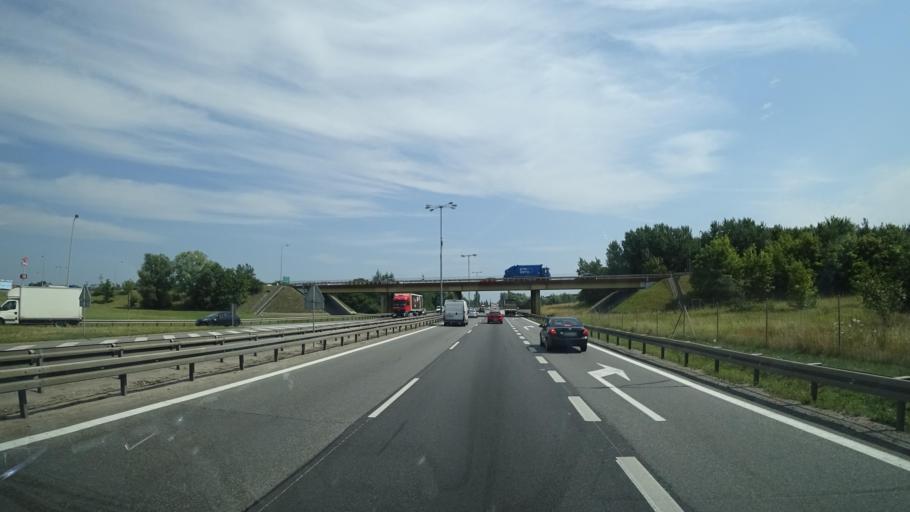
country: PL
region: Pomeranian Voivodeship
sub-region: Powiat gdanski
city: Kowale
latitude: 54.3077
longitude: 18.5564
